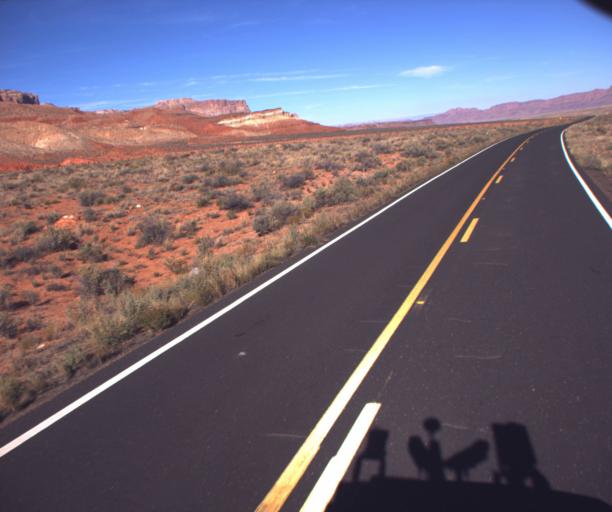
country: US
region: Arizona
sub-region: Coconino County
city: LeChee
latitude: 36.6963
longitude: -111.8086
